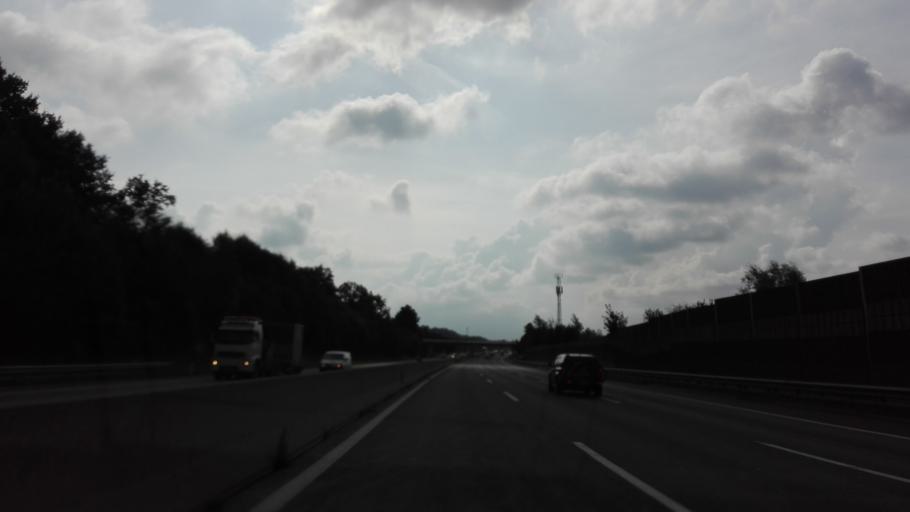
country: AT
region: Lower Austria
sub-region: Politischer Bezirk Melk
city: Blindenmarkt
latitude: 48.1356
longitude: 14.9820
